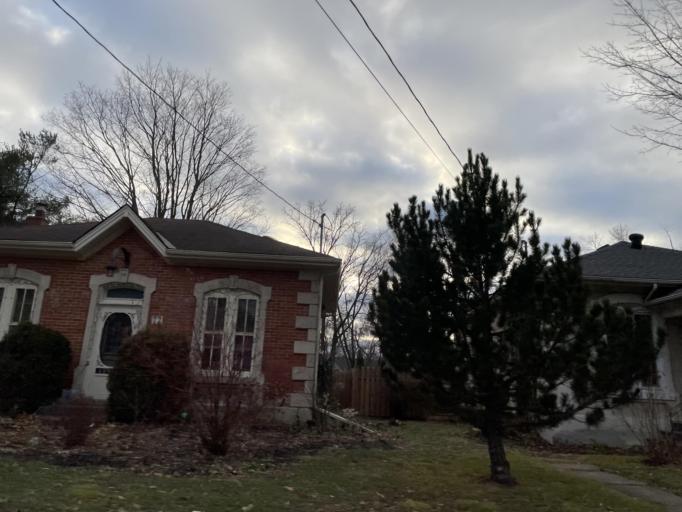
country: CA
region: Ontario
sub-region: Wellington County
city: Guelph
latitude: 43.5393
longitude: -80.2606
